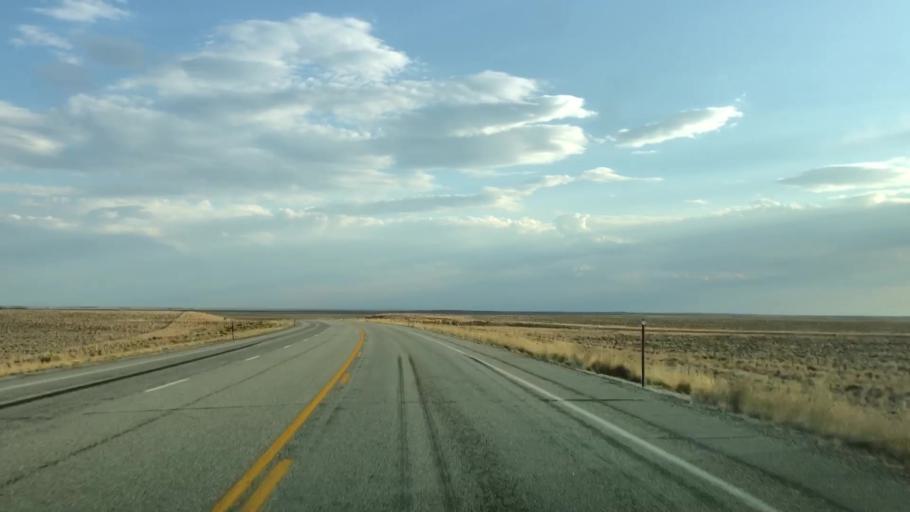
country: US
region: Wyoming
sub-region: Sweetwater County
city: North Rock Springs
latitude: 42.1957
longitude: -109.4804
